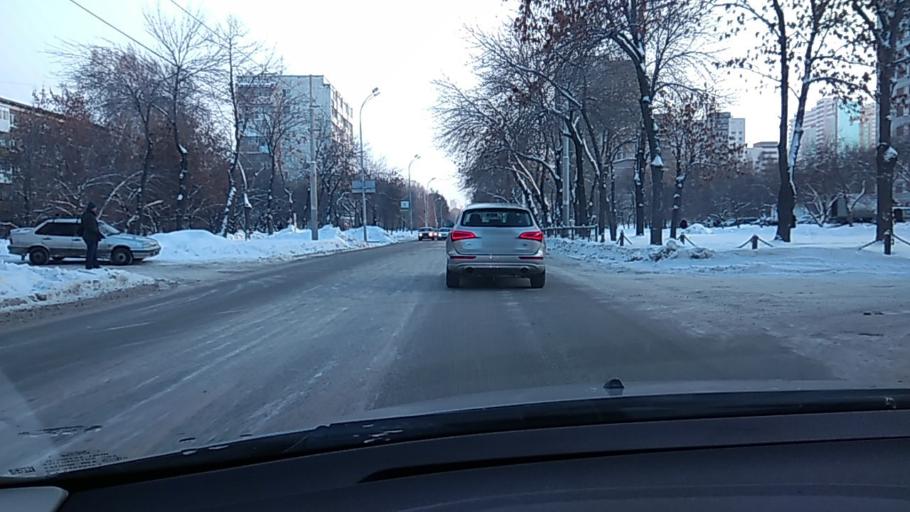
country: RU
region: Sverdlovsk
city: Sovkhoznyy
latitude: 56.8154
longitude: 60.5678
